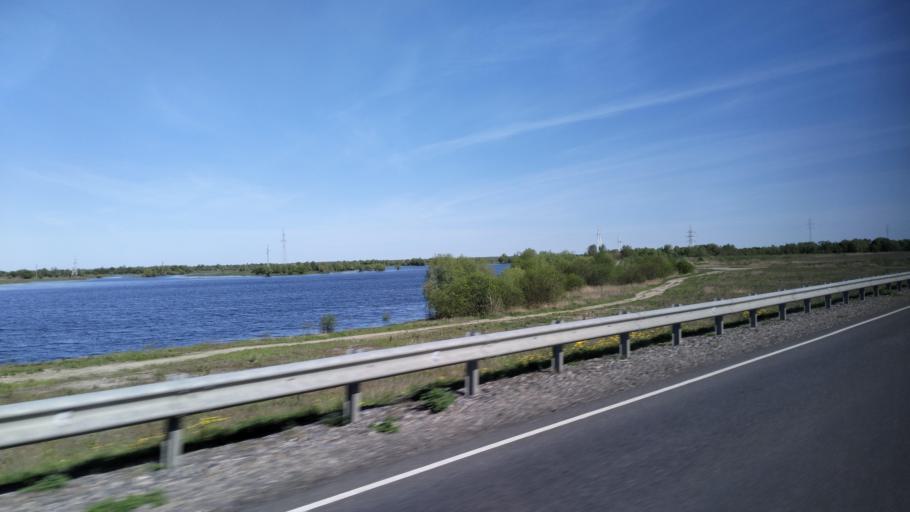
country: BY
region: Gomel
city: Turaw
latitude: 52.0698
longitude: 27.8240
